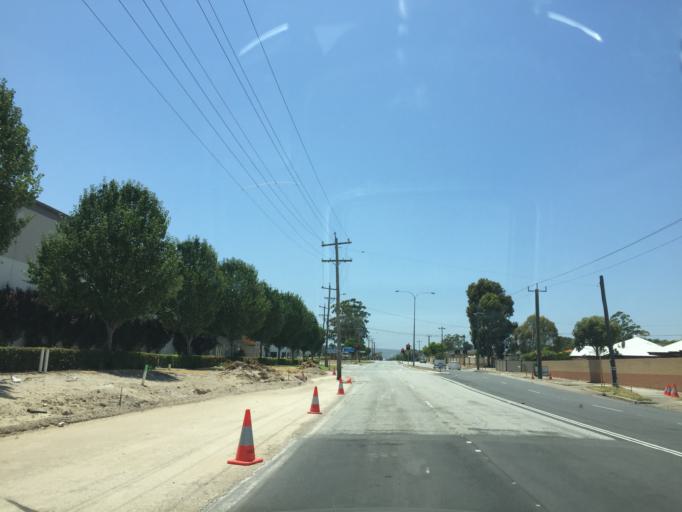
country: AU
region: Western Australia
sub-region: Canning
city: Queens Park
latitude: -31.9962
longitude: 115.9423
